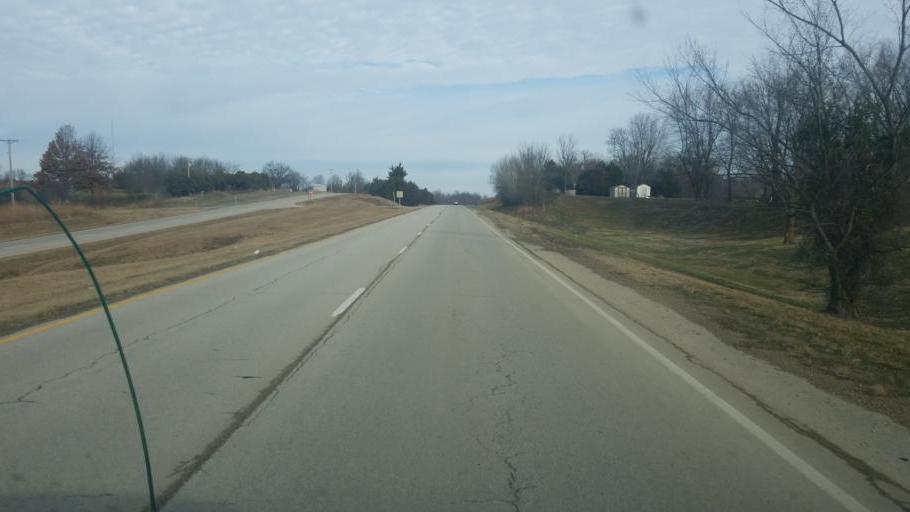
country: US
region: Missouri
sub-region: Stoddard County
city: Dexter
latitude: 36.8356
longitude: -89.9415
